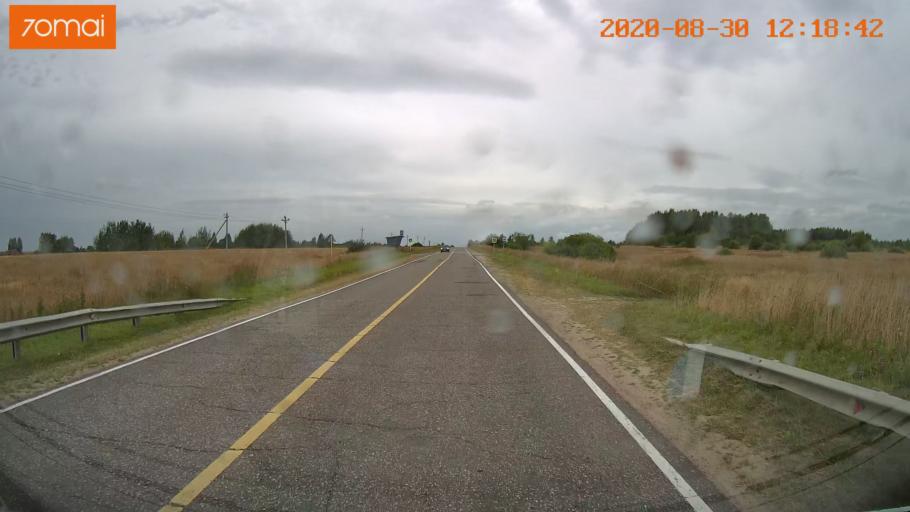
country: RU
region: Ivanovo
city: Yur'yevets
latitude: 57.3233
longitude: 42.9457
